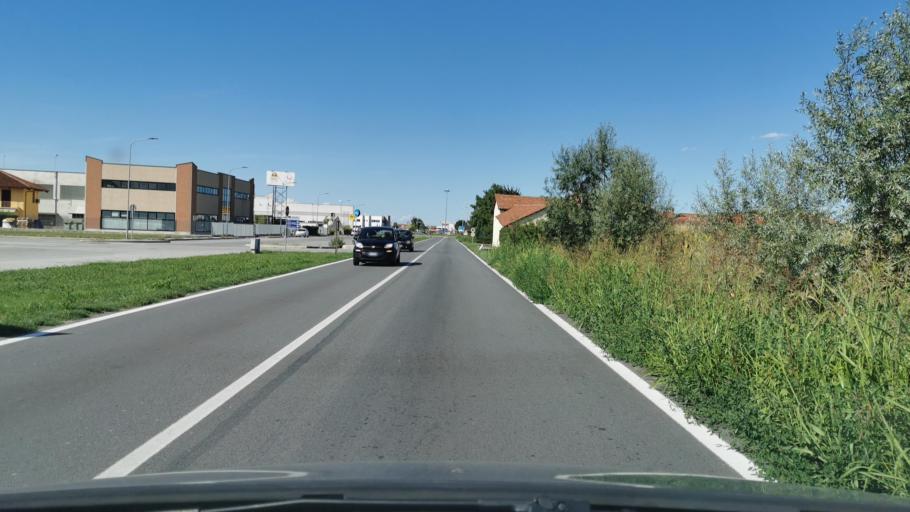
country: IT
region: Piedmont
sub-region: Provincia di Cuneo
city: Genola
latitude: 44.5901
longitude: 7.6561
